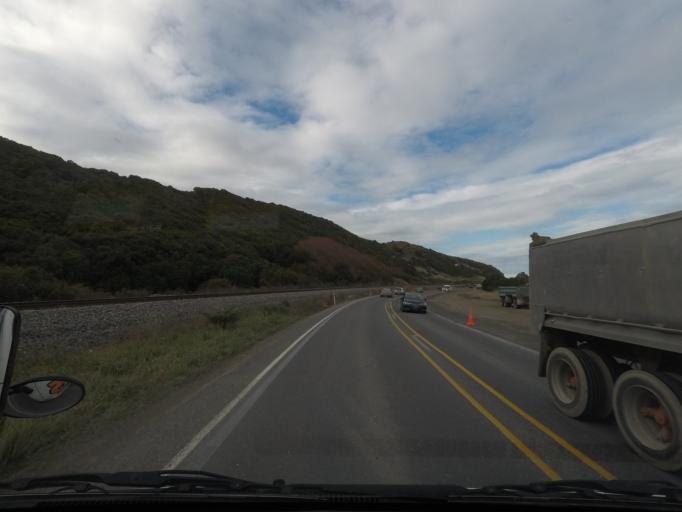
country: NZ
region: Canterbury
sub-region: Kaikoura District
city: Kaikoura
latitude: -42.2164
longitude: 173.8618
